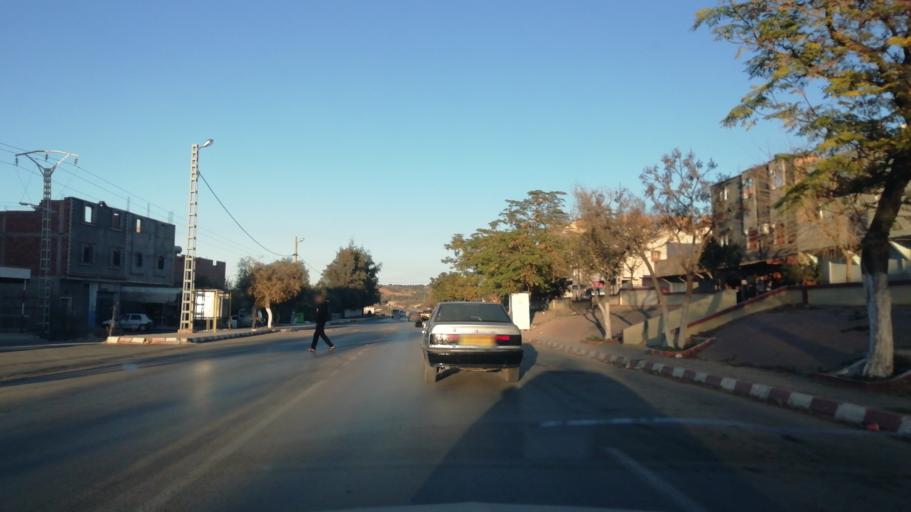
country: DZ
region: Tlemcen
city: Nedroma
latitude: 34.8514
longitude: -1.6850
